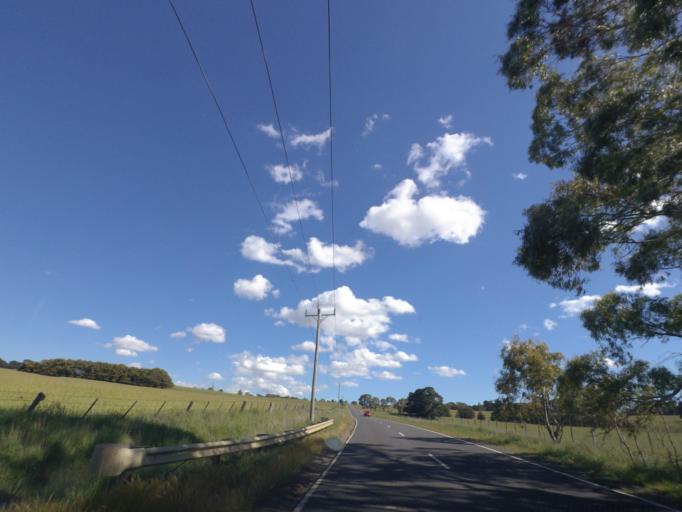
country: AU
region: Victoria
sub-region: Moorabool
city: Bacchus Marsh
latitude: -37.6026
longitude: 144.3193
